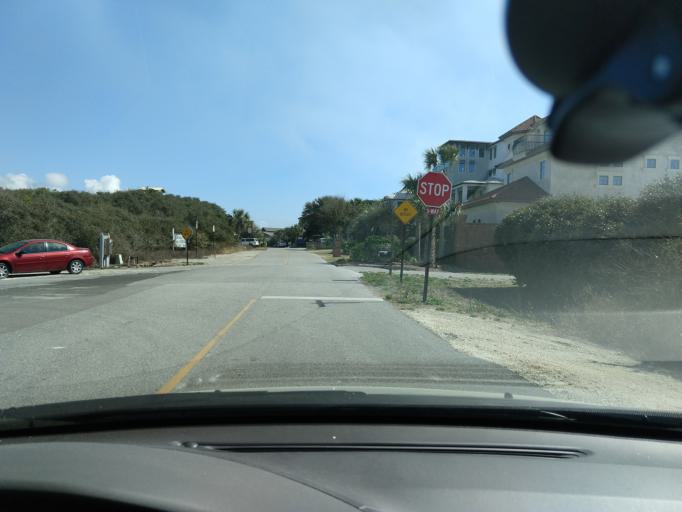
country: US
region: Florida
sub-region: Walton County
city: Seaside
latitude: 30.3365
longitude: -86.1943
